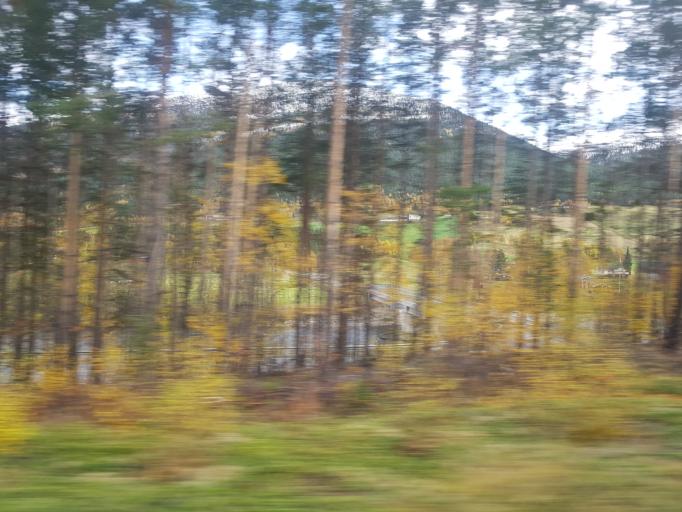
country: NO
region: Oppland
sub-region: Dovre
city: Dovre
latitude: 61.9330
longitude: 9.3124
